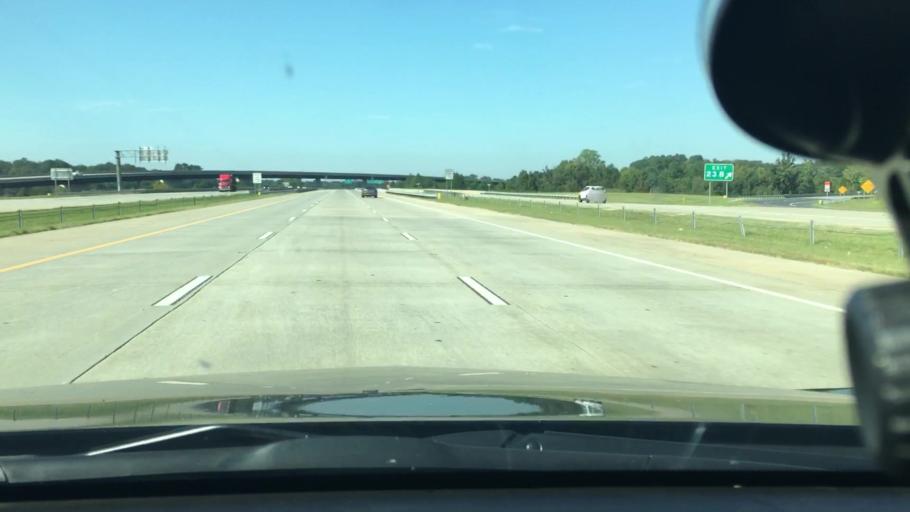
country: US
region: North Carolina
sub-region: Mecklenburg County
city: Huntersville
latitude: 35.3646
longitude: -80.8361
